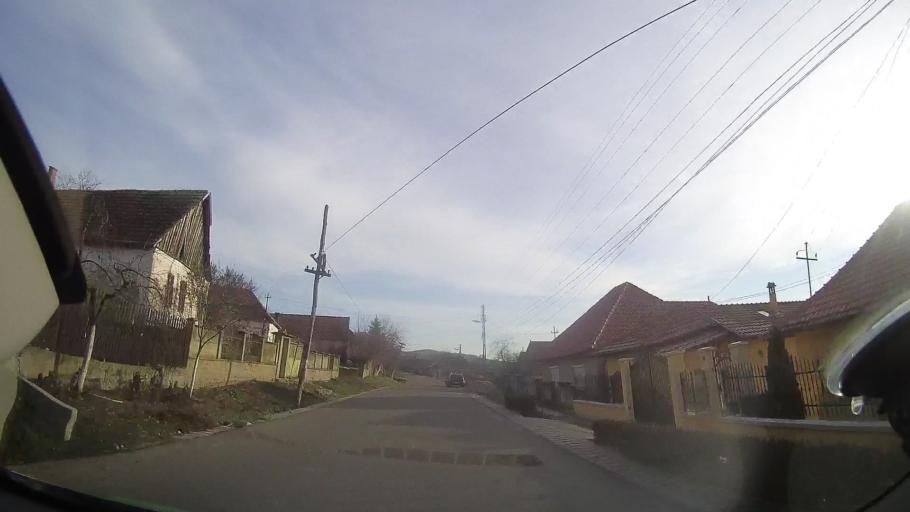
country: RO
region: Bihor
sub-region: Comuna Sarbi
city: Burzuc
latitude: 47.1732
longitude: 22.1538
